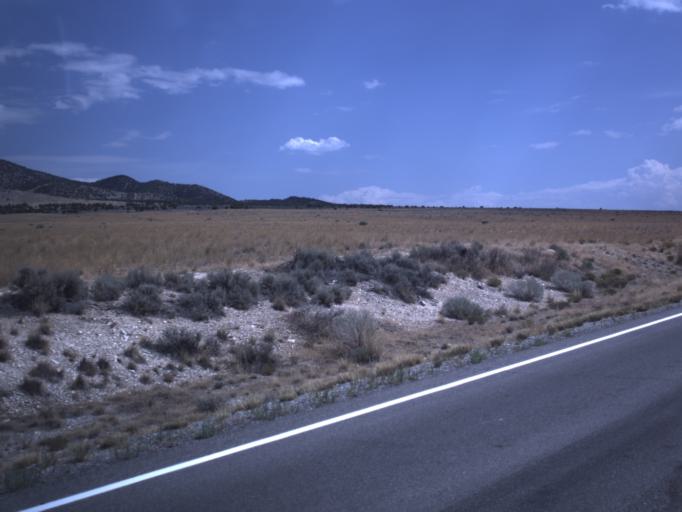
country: US
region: Utah
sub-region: Utah County
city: Eagle Mountain
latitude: 40.2717
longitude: -112.2459
